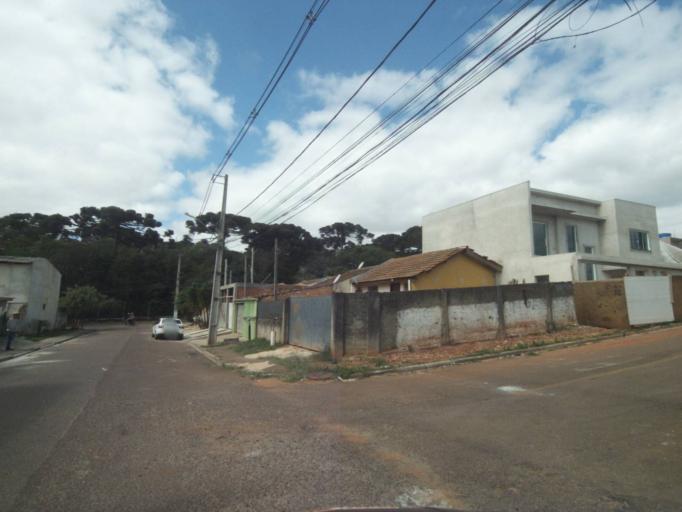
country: BR
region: Parana
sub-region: Sao Jose Dos Pinhais
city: Sao Jose dos Pinhais
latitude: -25.5576
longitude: -49.2616
